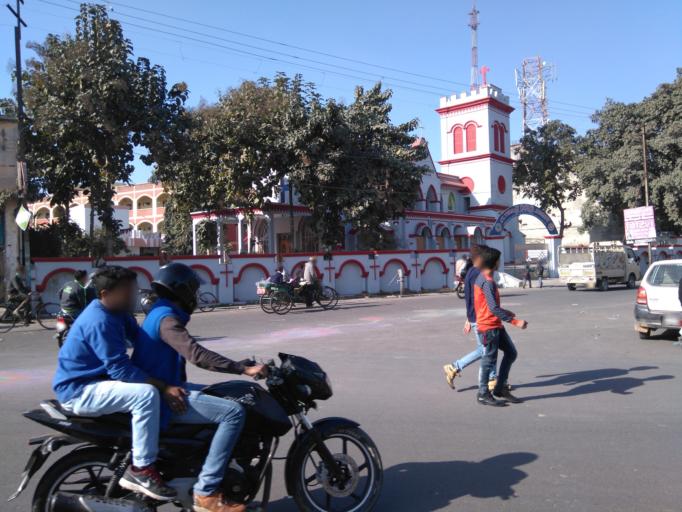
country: IN
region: Uttar Pradesh
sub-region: Meerut
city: Meerut
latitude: 28.9844
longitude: 77.7060
